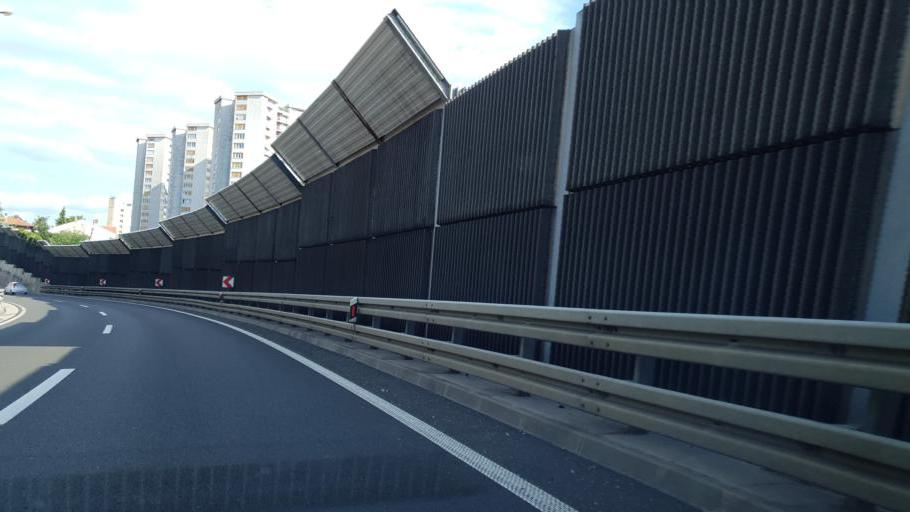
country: HR
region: Primorsko-Goranska
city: Drenova
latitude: 45.3348
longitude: 14.4450
